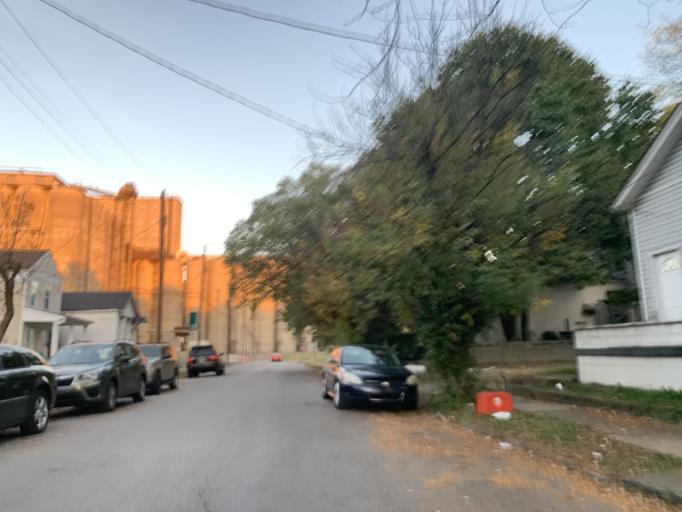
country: US
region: Kentucky
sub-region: Jefferson County
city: Louisville
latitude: 38.2385
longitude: -85.7793
